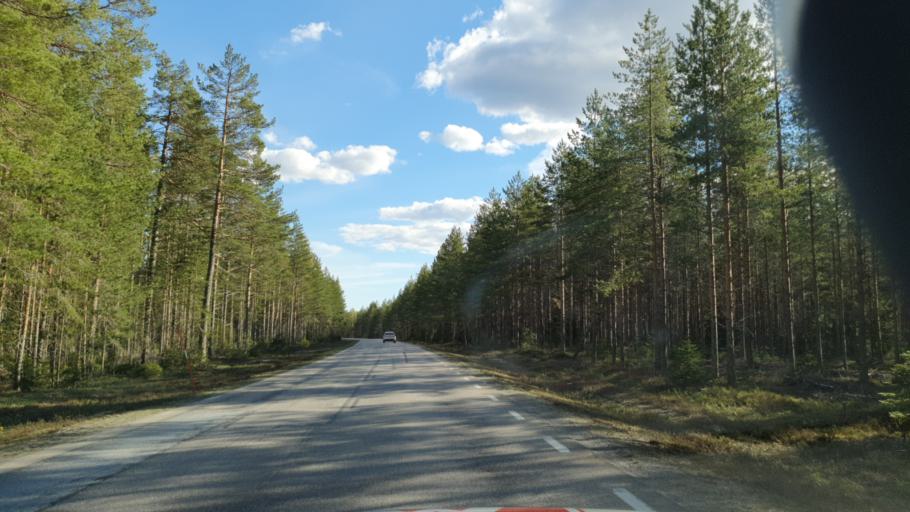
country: SE
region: Vaesterbotten
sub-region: Umea Kommun
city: Roback
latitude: 63.8667
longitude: 20.1455
